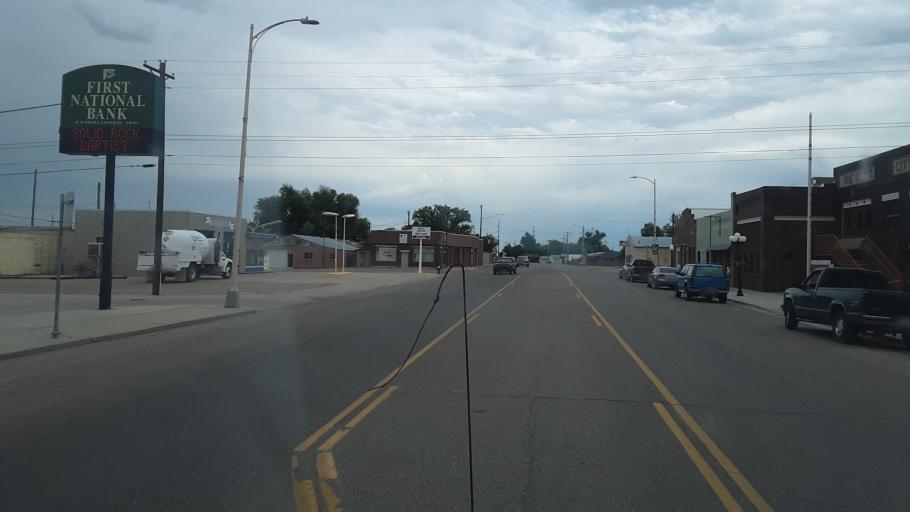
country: US
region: Colorado
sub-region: Otero County
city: Fowler
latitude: 38.1308
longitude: -104.0234
